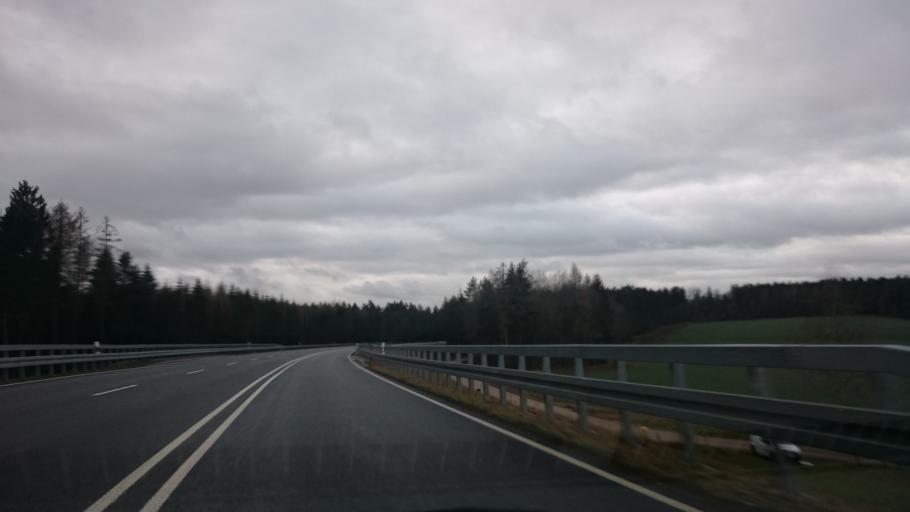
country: DE
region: Saxony
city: Kirchberg
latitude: 50.6095
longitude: 12.5828
